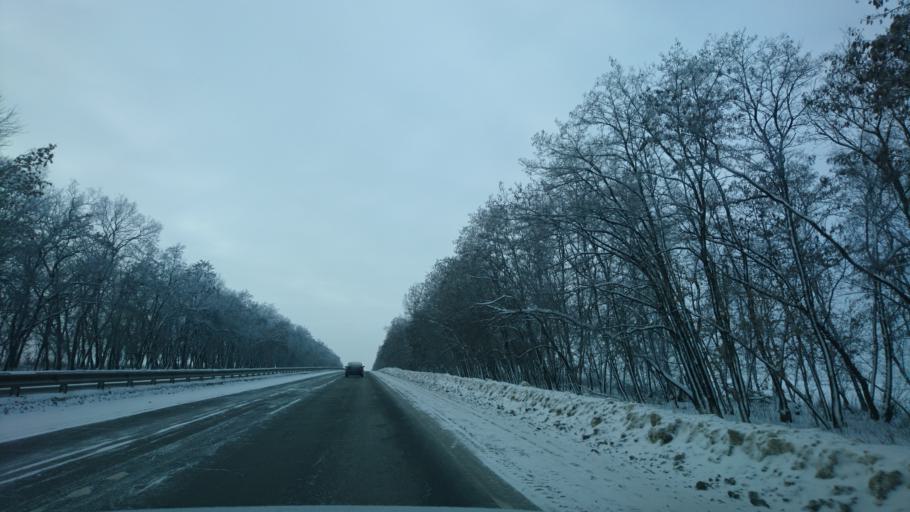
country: RU
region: Belgorod
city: Mayskiy
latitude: 50.4926
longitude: 36.4222
